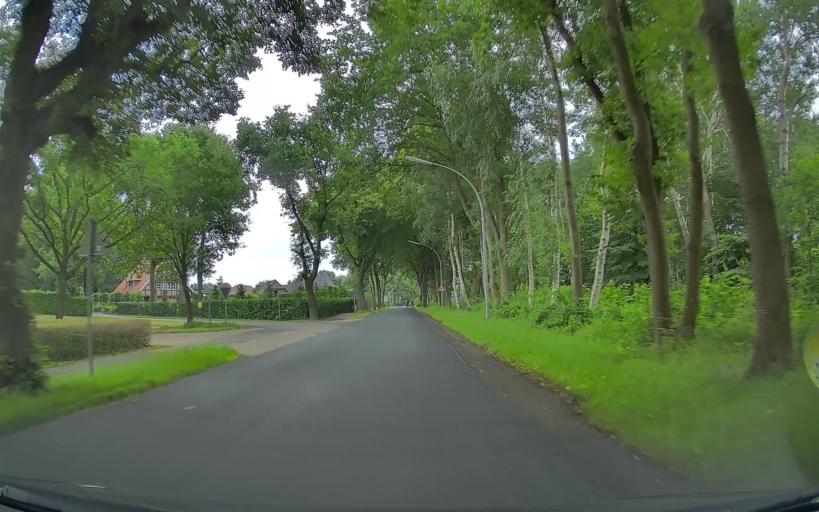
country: DE
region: Lower Saxony
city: Bosel
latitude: 52.9986
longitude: 7.9498
